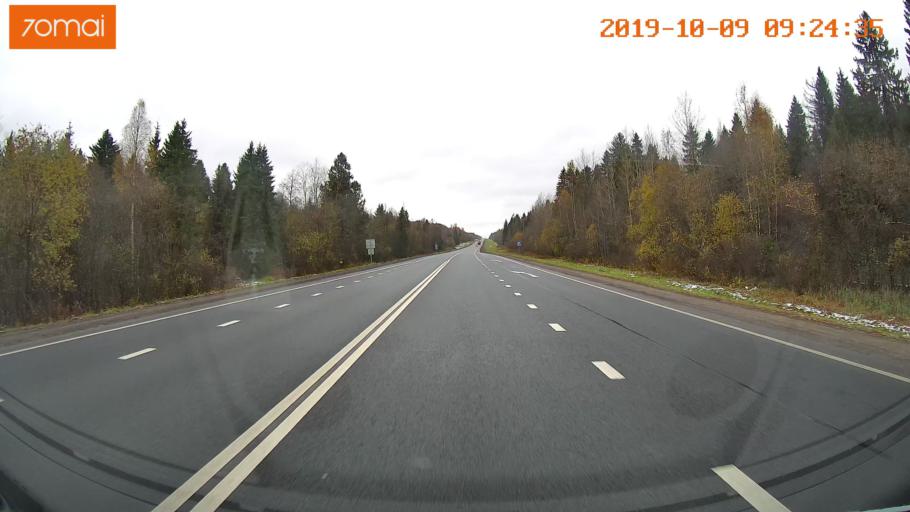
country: RU
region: Vologda
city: Vologda
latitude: 59.0805
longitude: 40.0141
